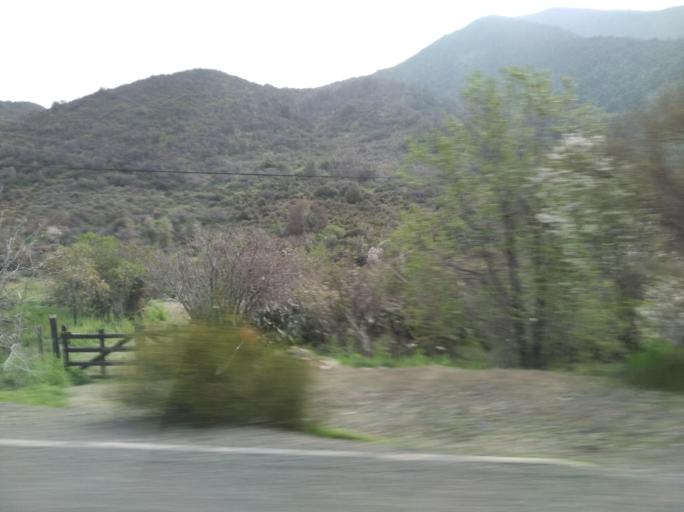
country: CL
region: Santiago Metropolitan
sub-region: Provincia de Chacabuco
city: Lampa
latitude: -33.0729
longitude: -70.9634
